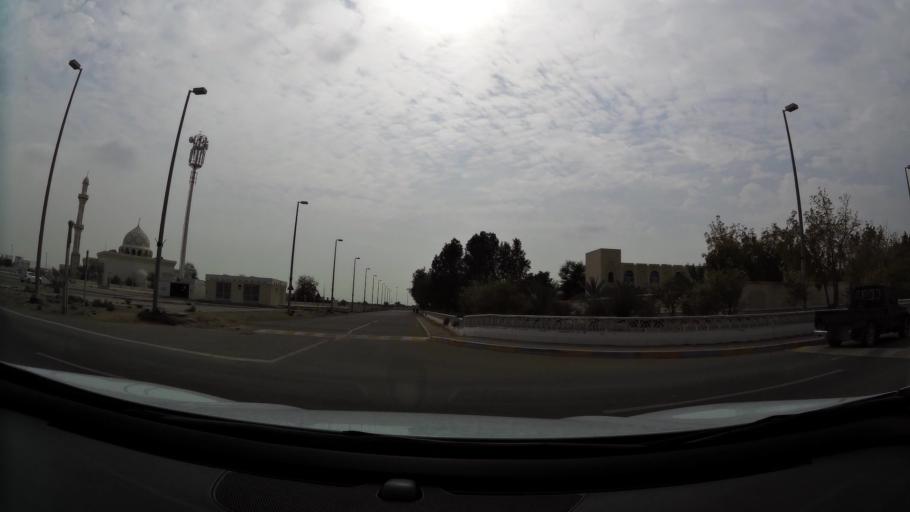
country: AE
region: Abu Dhabi
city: Abu Dhabi
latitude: 24.6468
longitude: 54.7325
